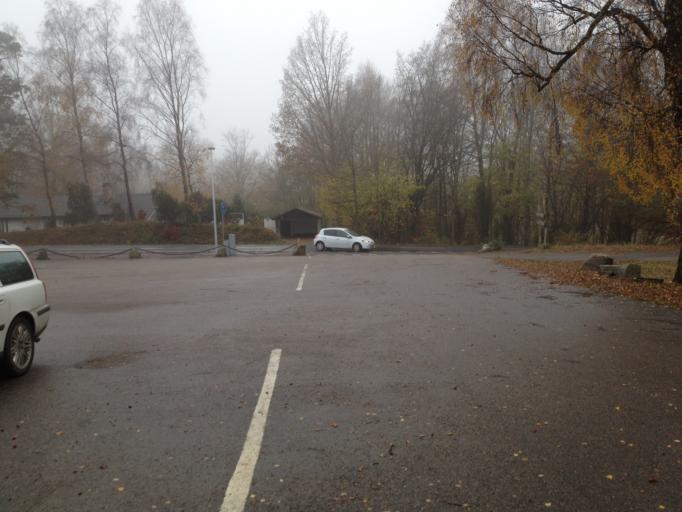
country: SE
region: Skane
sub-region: Hoors Kommun
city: Hoeoer
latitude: 55.9684
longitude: 13.5181
